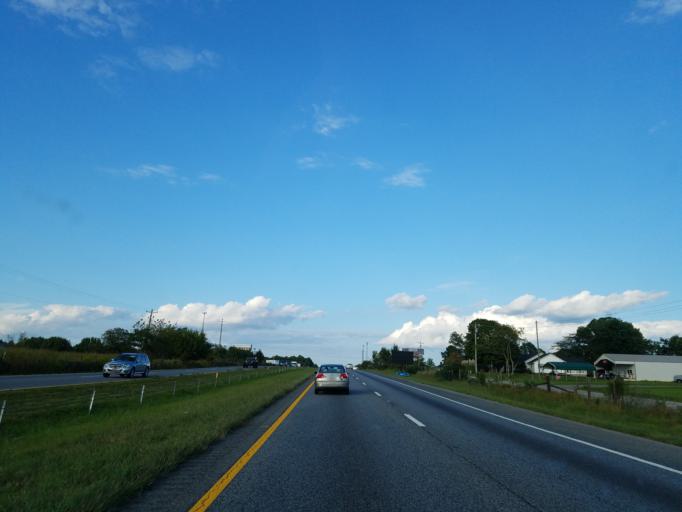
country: US
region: South Carolina
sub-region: Spartanburg County
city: Cowpens
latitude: 35.0632
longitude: -81.7748
